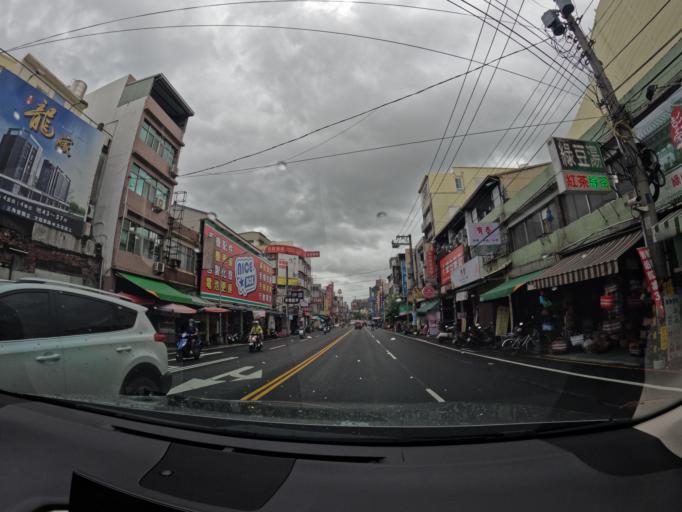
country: TW
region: Taiwan
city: Fengshan
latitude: 22.6259
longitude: 120.3598
